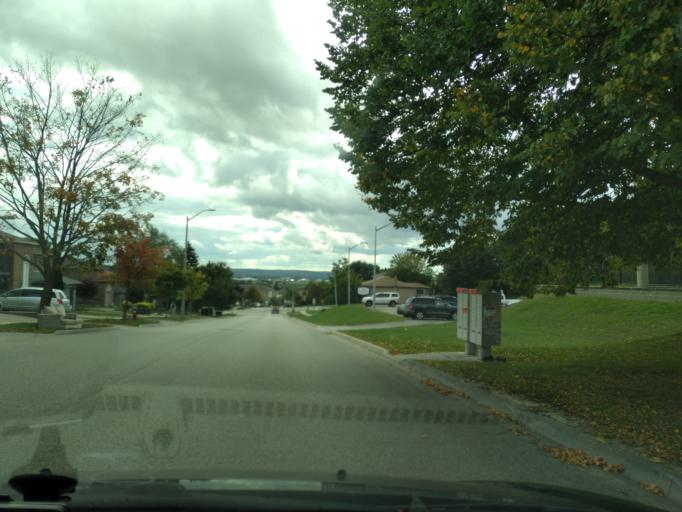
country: CA
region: Ontario
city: Bradford West Gwillimbury
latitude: 44.1226
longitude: -79.5631
